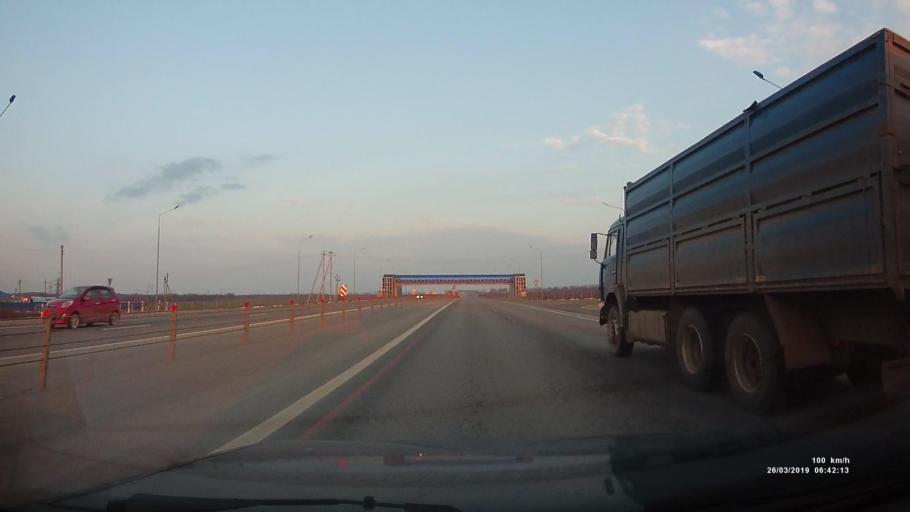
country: RU
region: Rostov
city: Sinyavskoye
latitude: 47.2905
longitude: 39.3060
